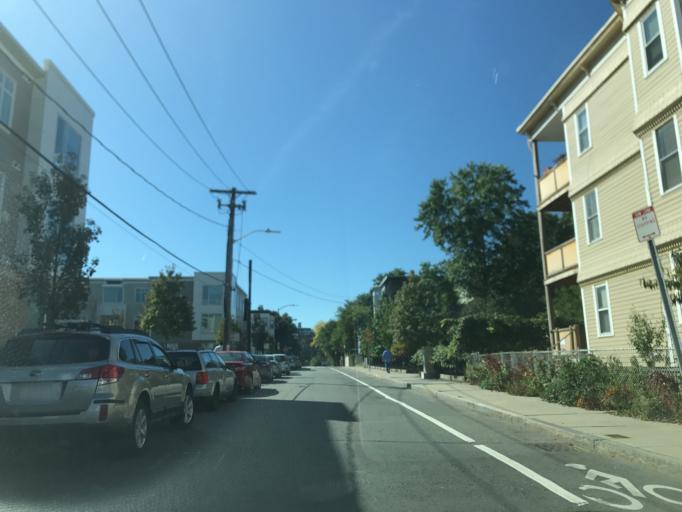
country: US
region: Massachusetts
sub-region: Middlesex County
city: Cambridge
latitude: 42.3574
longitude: -71.1060
